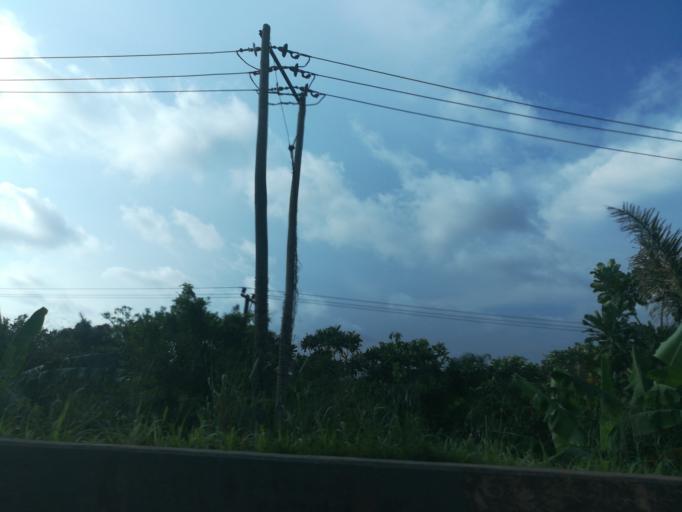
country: NG
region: Ogun
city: Ado Odo
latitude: 6.4925
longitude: 3.0797
